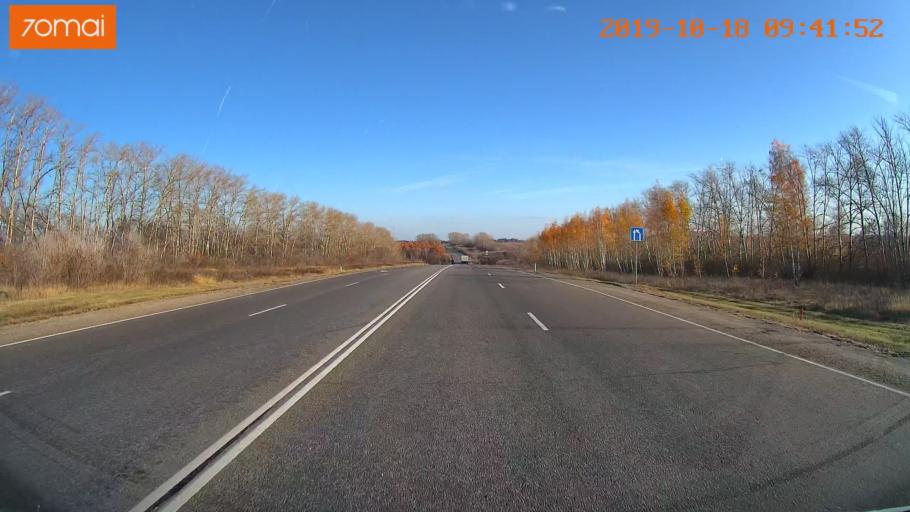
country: RU
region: Tula
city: Kazachka
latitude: 53.2799
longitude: 38.1681
